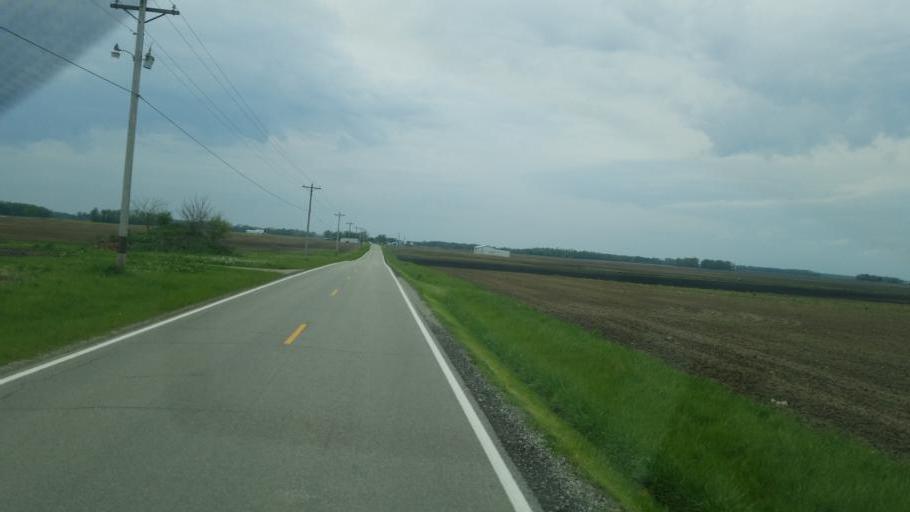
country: US
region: Ohio
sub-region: Huron County
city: Willard
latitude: 40.9820
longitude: -82.7543
